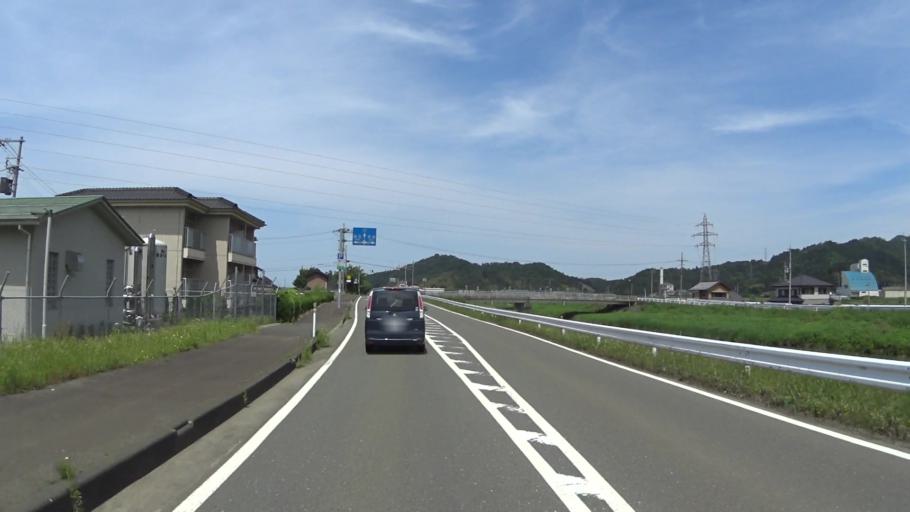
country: JP
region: Fukui
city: Obama
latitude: 35.4640
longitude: 135.6147
